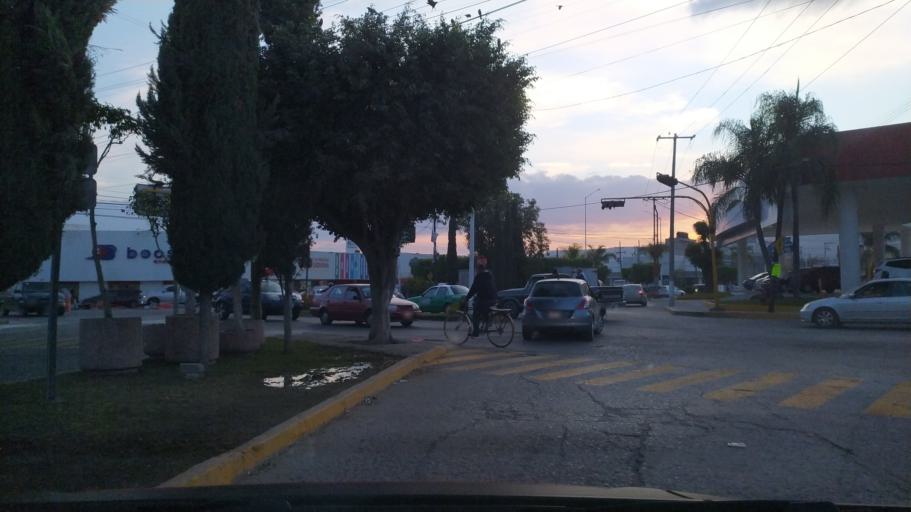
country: MX
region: Guanajuato
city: San Francisco del Rincon
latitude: 21.0294
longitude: -101.8527
